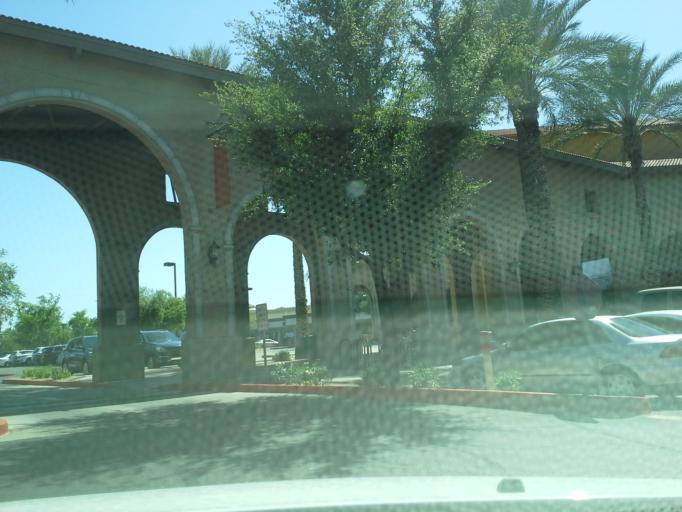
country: US
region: Arizona
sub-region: Maricopa County
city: Paradise Valley
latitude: 33.5847
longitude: -111.9227
